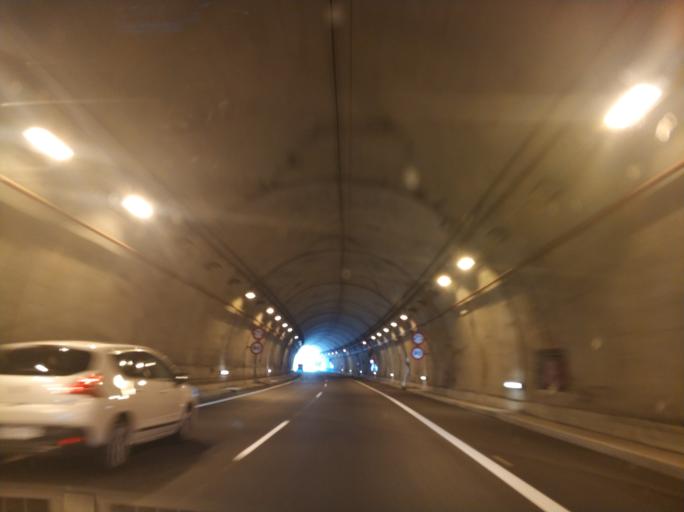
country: ES
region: Asturias
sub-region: Province of Asturias
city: Cudillero
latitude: 43.5427
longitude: -6.1540
